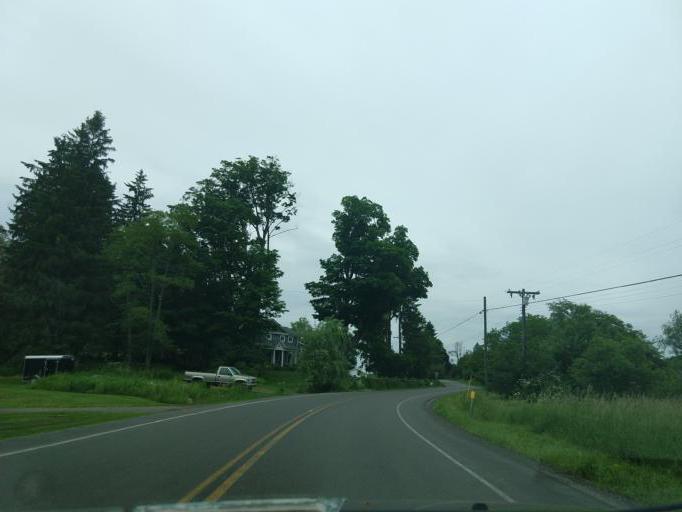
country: US
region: New York
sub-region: Cortland County
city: Munsons Corners
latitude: 42.5024
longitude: -76.2025
